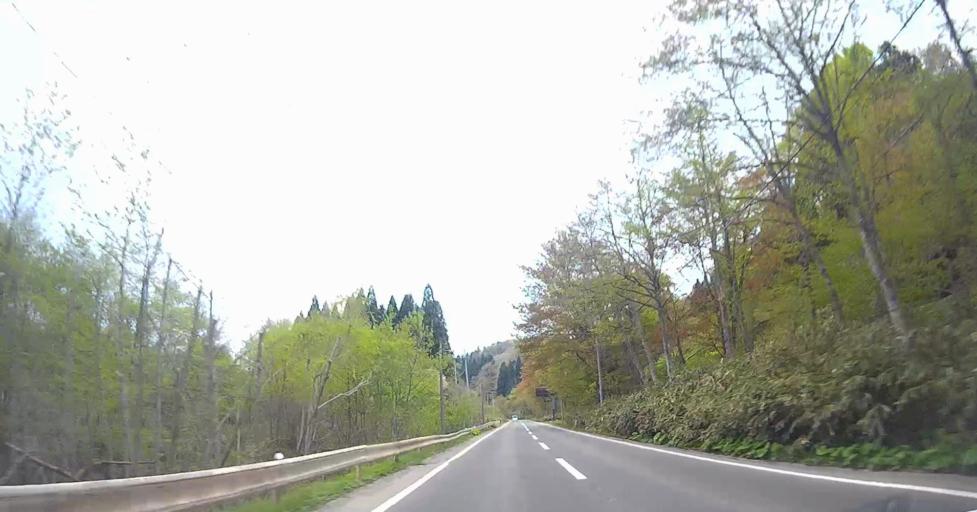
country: JP
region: Aomori
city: Goshogawara
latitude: 41.1280
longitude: 140.5198
